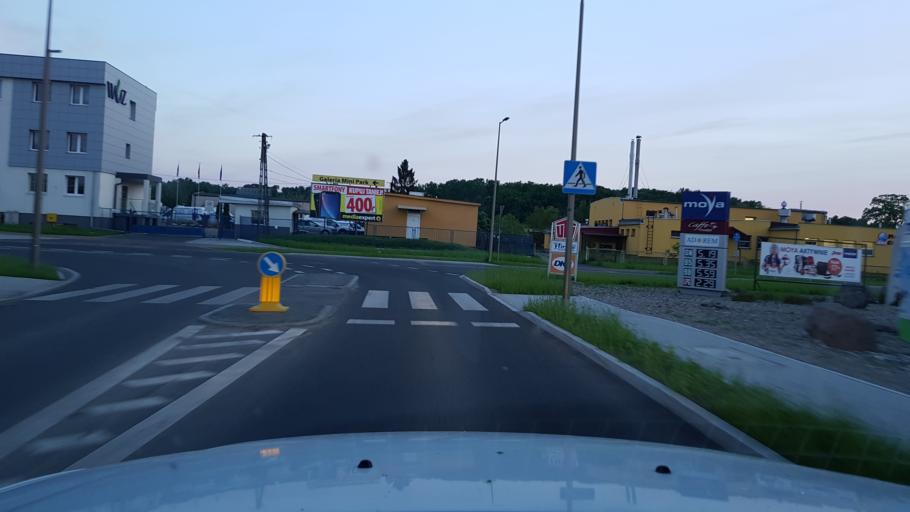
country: PL
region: West Pomeranian Voivodeship
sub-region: Powiat goleniowski
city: Goleniow
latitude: 53.5587
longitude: 14.8448
